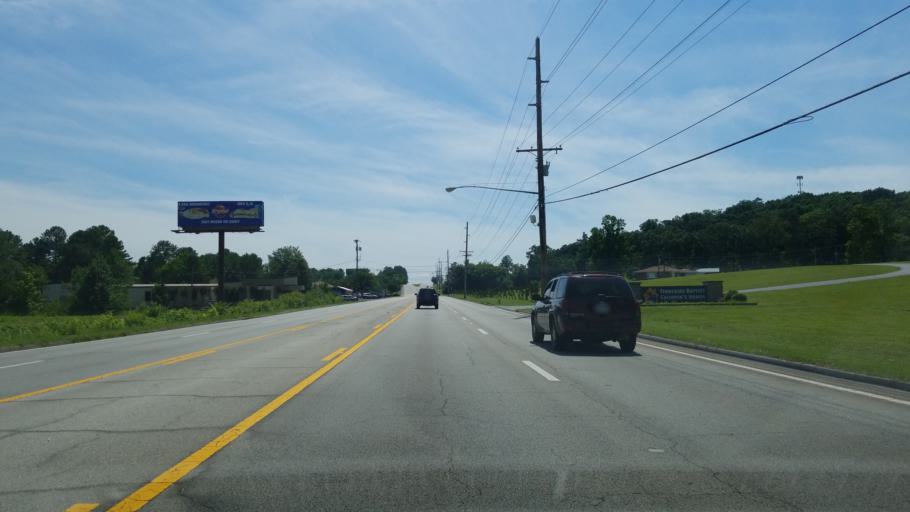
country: US
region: Tennessee
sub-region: Hamilton County
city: East Brainerd
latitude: 35.0389
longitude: -85.1722
